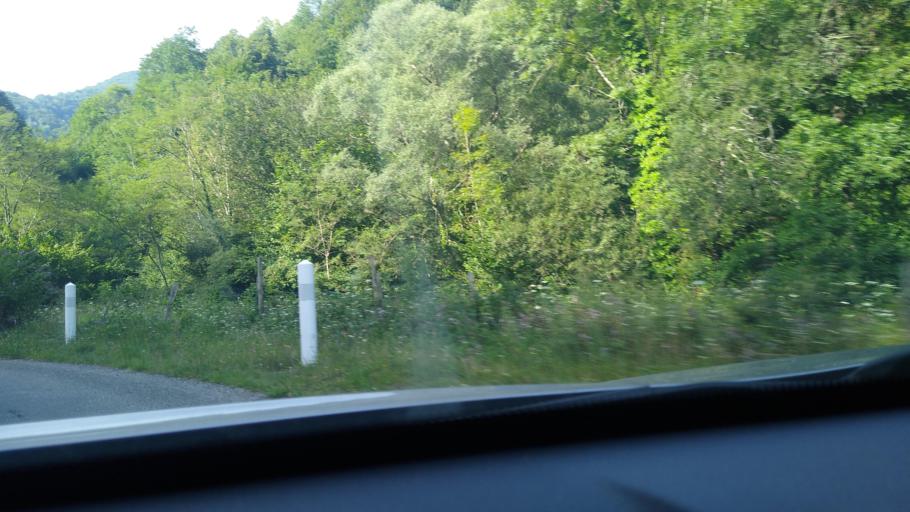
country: FR
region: Midi-Pyrenees
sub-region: Departement de l'Ariege
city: Saint-Girons
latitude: 42.8489
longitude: 1.1914
